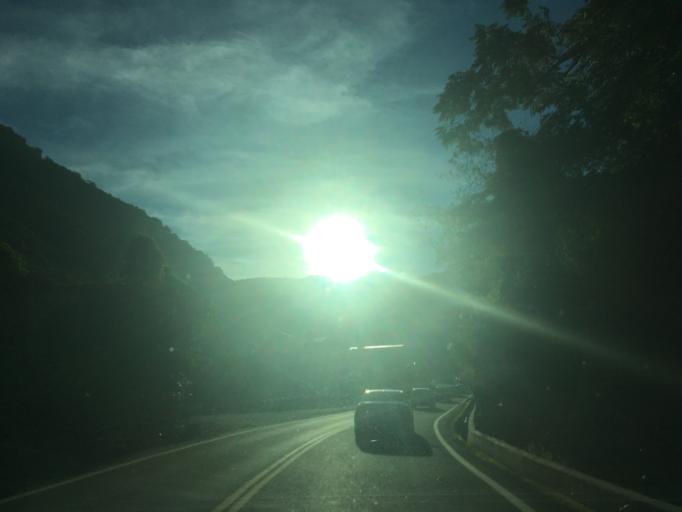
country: TW
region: Taiwan
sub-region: Nantou
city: Puli
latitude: 24.0035
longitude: 121.0554
